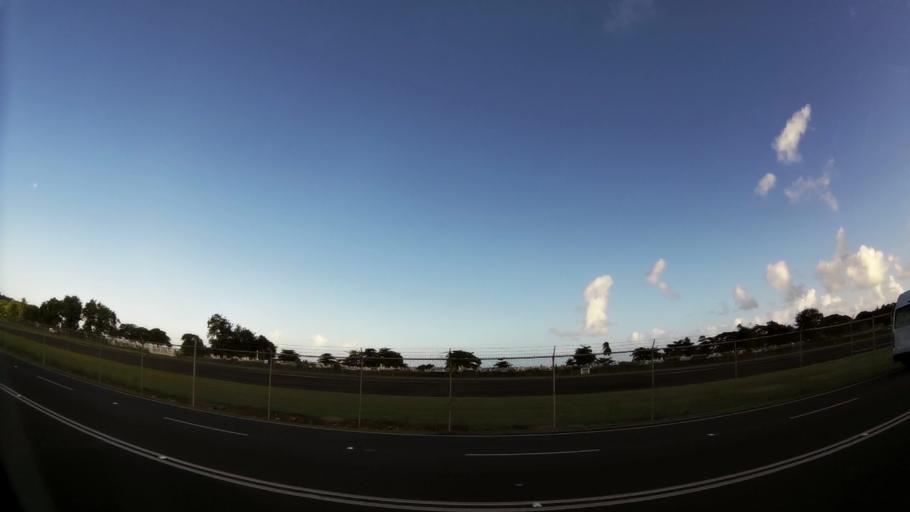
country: LC
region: Castries Quarter
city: Bisee
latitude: 14.0213
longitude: -60.9862
